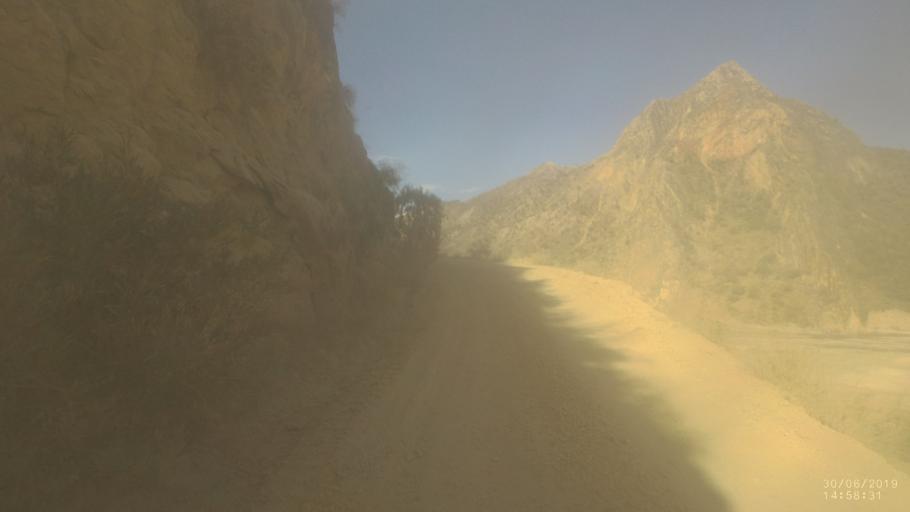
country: BO
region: Cochabamba
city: Irpa Irpa
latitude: -17.7385
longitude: -66.3488
